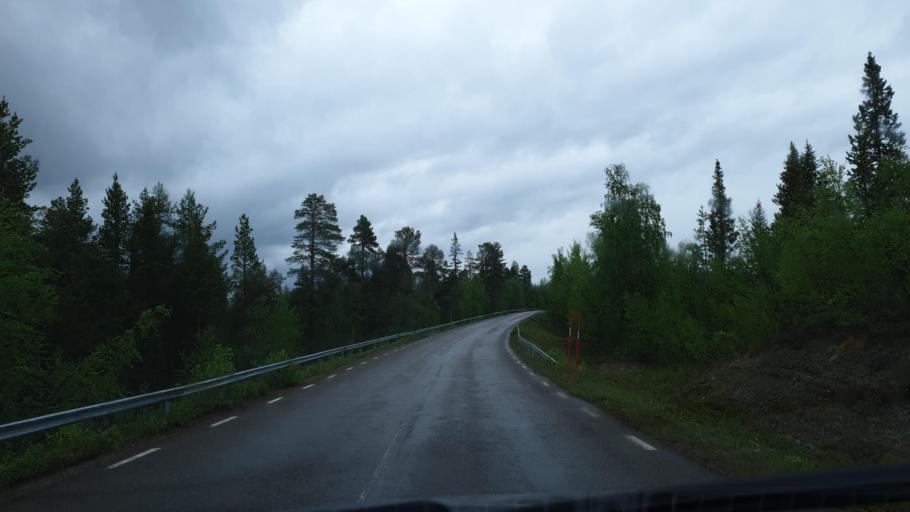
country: SE
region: Norrbotten
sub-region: Kiruna Kommun
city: Kiruna
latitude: 67.8859
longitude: 21.0115
